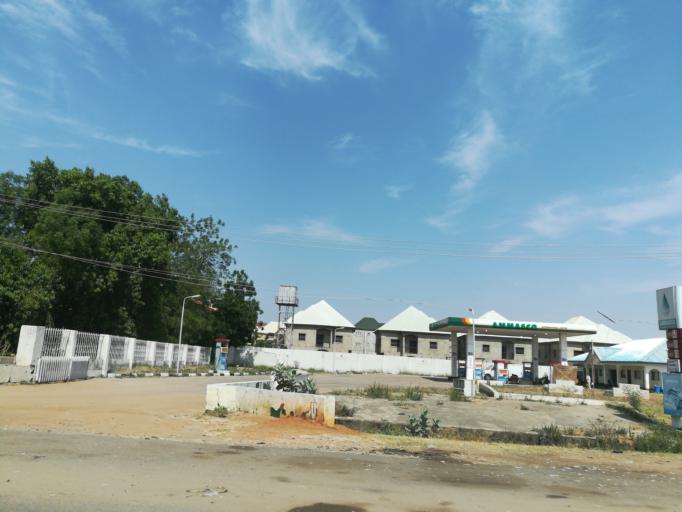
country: NG
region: Kano
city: Kano
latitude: 12.0289
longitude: 8.5210
